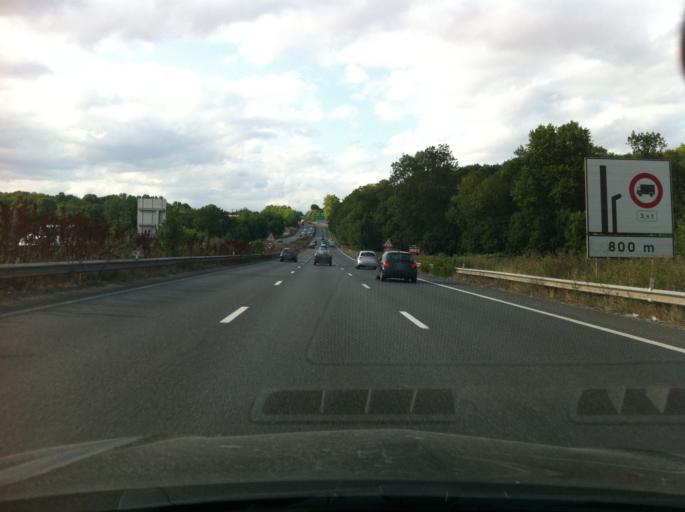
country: FR
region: Ile-de-France
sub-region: Departement de Seine-et-Marne
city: Brie-Comte-Robert
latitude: 48.6690
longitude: 2.6123
